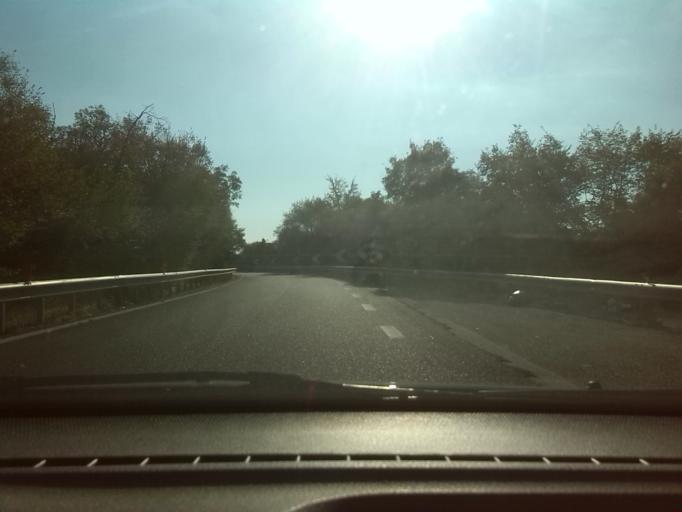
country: IT
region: Friuli Venezia Giulia
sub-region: Provincia di Trieste
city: Sistiana-Visogliano
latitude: 45.7629
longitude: 13.6408
